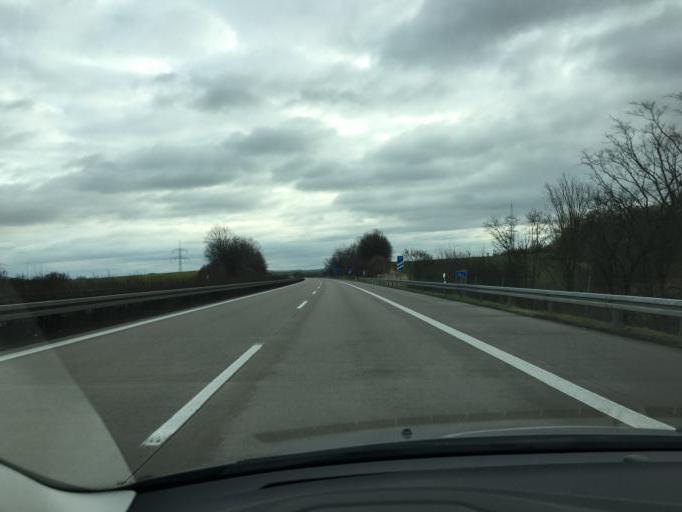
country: DE
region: Saxony
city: Dobeln
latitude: 51.1587
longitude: 13.1098
